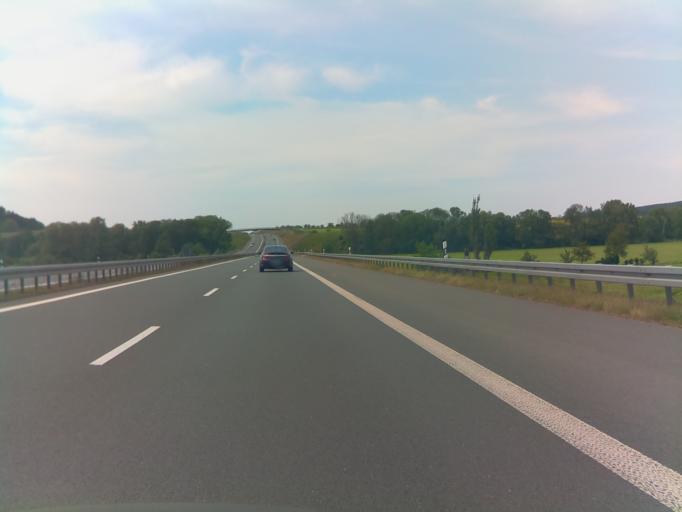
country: DE
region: Saxony-Anhalt
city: Ditfurt
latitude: 51.8089
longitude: 11.1854
